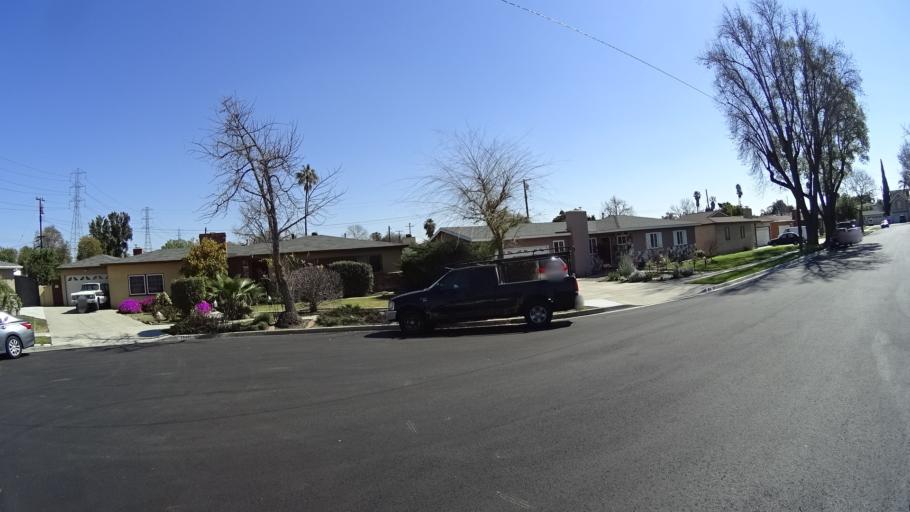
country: US
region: California
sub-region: Orange County
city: Garden Grove
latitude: 33.8063
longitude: -117.9454
